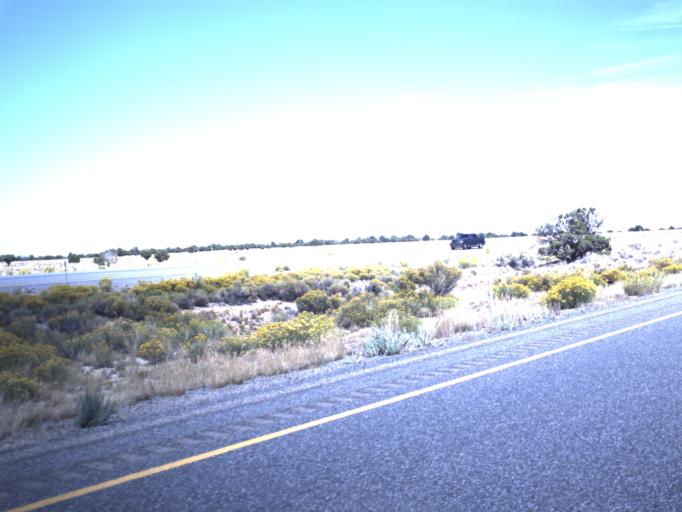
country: US
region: Utah
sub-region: Emery County
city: Castle Dale
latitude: 38.8969
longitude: -110.5985
